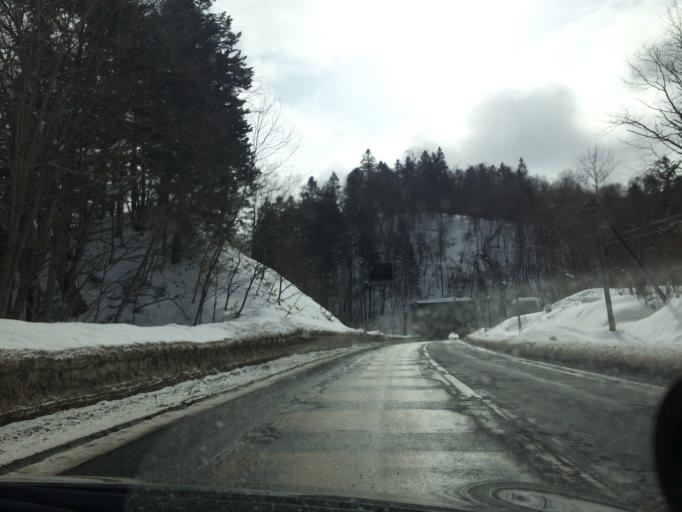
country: JP
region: Hokkaido
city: Iwamizawa
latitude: 42.9262
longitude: 142.1159
